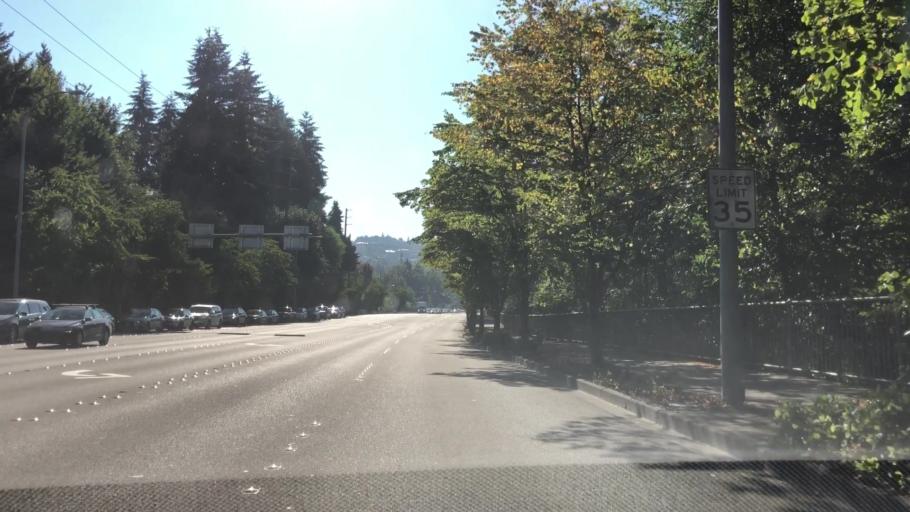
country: US
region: Washington
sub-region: King County
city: Newport
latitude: 47.5668
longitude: -122.1780
